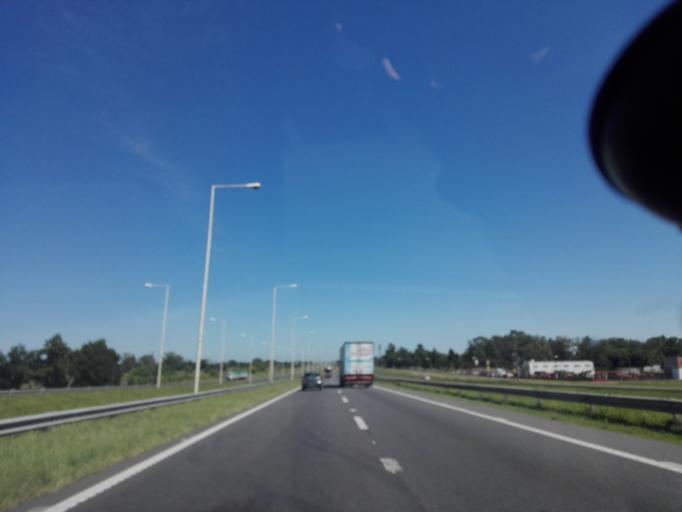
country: AR
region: Buenos Aires
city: San Nicolas de los Arroyos
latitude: -33.3881
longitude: -60.2222
